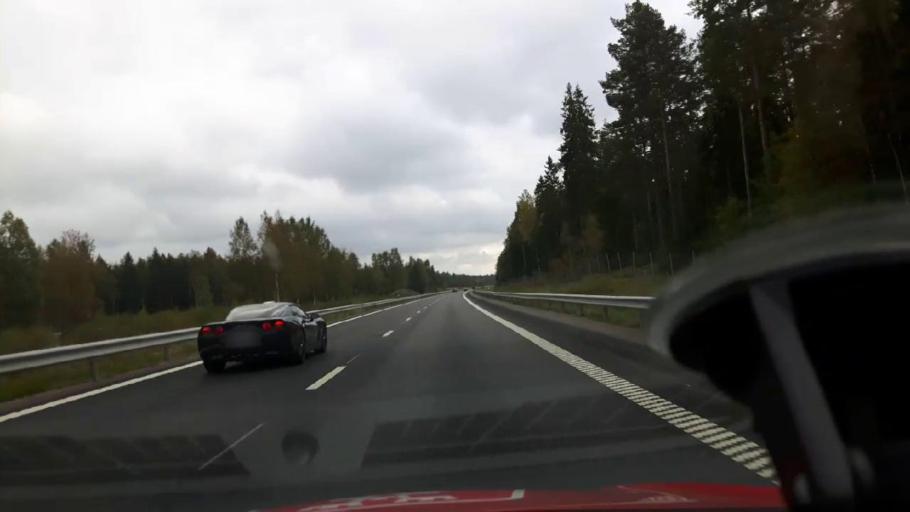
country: SE
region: Gaevleborg
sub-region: Gavle Kommun
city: Gavle
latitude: 60.6087
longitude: 17.1756
